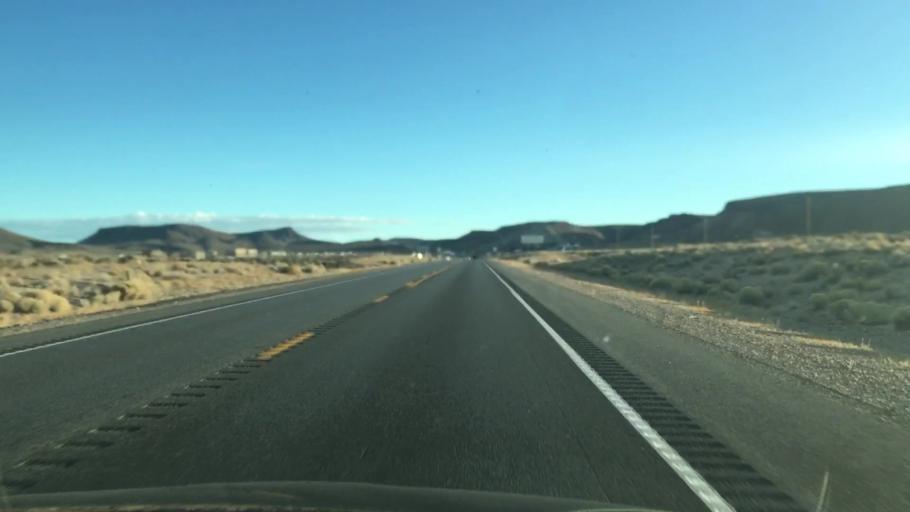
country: US
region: Nevada
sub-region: Esmeralda County
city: Goldfield
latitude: 37.7236
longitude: -117.2435
